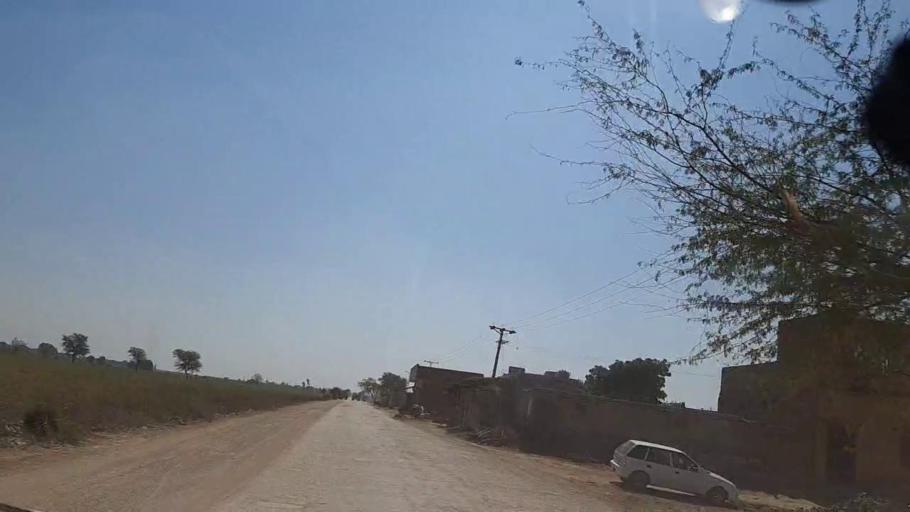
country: PK
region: Sindh
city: Mirpur Khas
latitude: 25.5041
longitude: 69.0326
